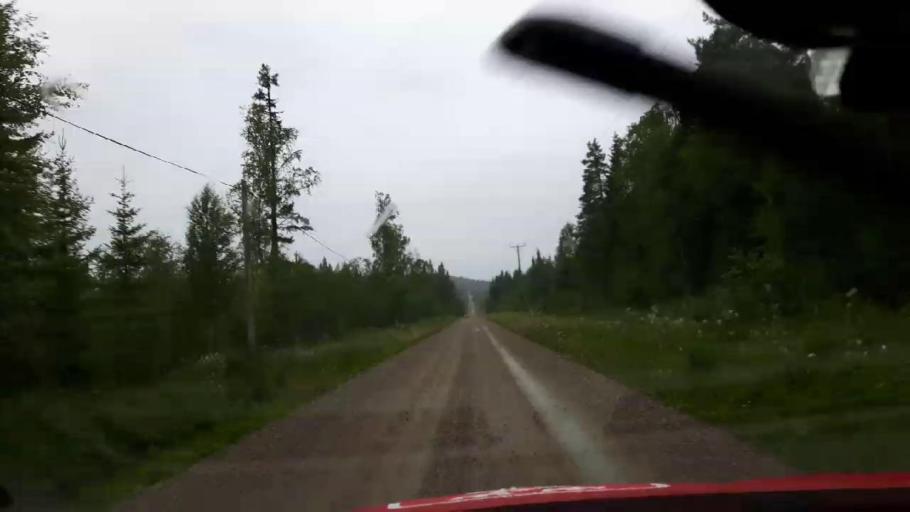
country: SE
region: Jaemtland
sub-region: OEstersunds Kommun
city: Brunflo
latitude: 62.7755
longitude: 14.9886
